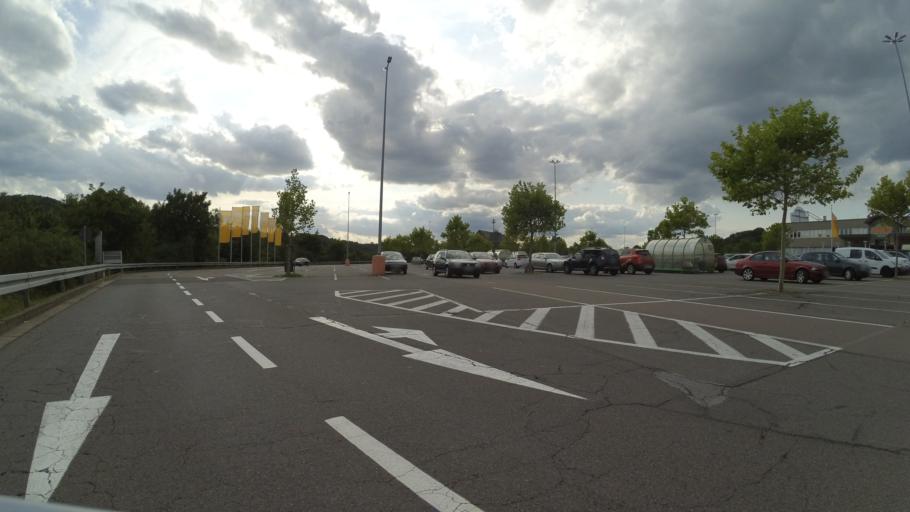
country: DE
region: Rheinland-Pfalz
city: Zweibrucken
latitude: 49.2620
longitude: 7.3346
